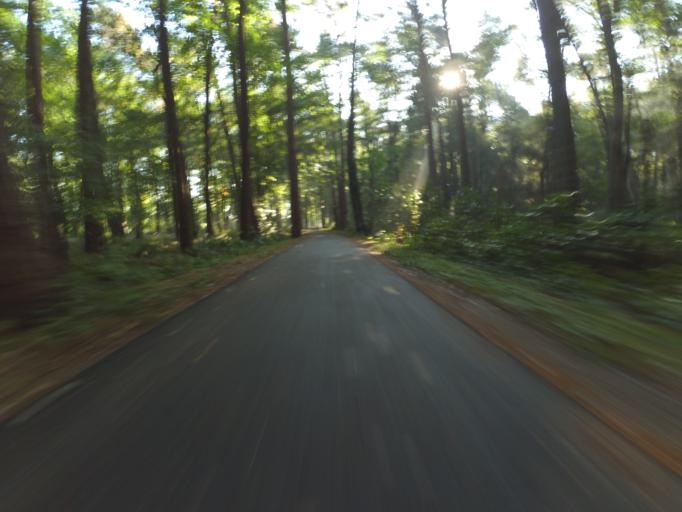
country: NL
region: Gelderland
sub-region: Gemeente Apeldoorn
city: Apeldoorn
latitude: 52.2464
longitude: 5.9457
